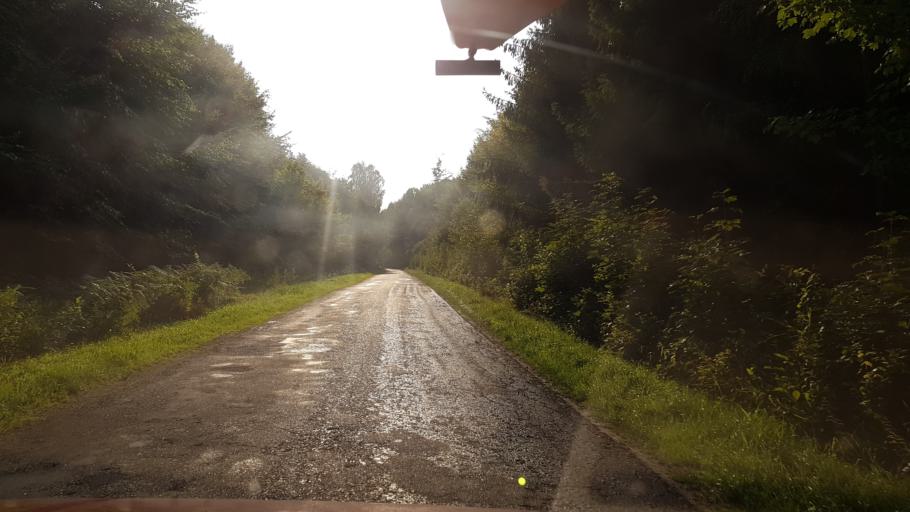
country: PL
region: Pomeranian Voivodeship
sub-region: Powiat bytowski
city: Miastko
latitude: 53.9818
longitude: 16.8889
